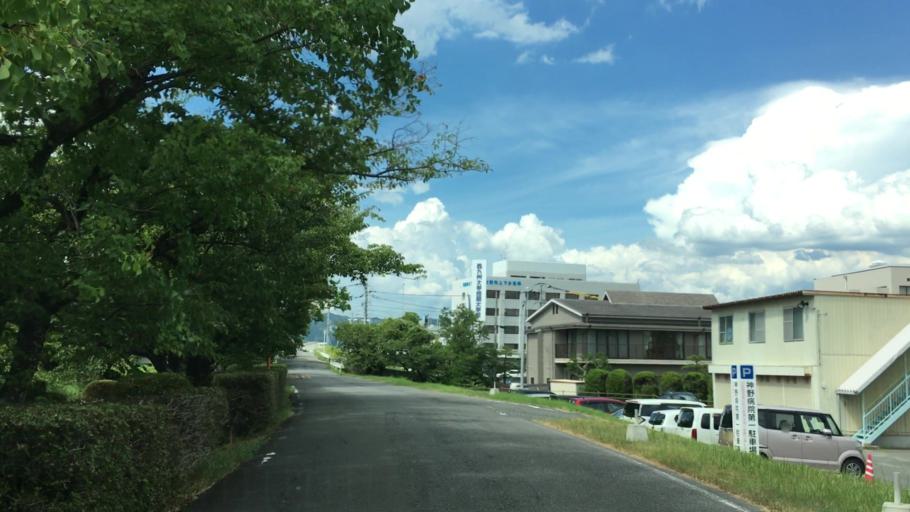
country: JP
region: Saga Prefecture
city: Saga-shi
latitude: 33.2717
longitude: 130.2825
